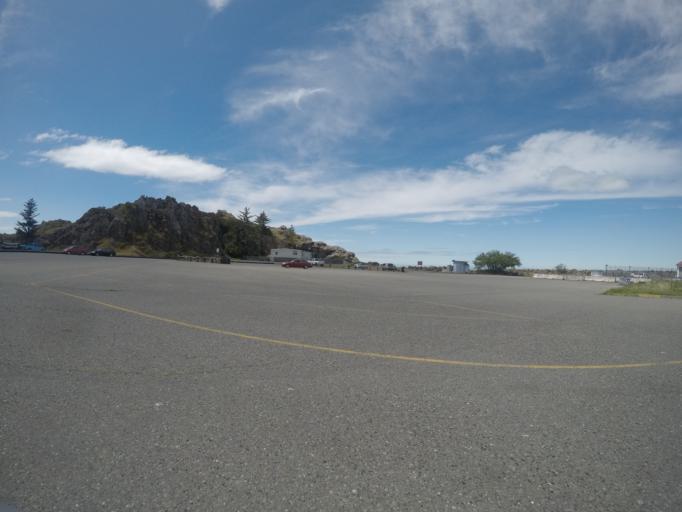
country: US
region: California
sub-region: Del Norte County
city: Crescent City
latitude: 41.7408
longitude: -124.1837
